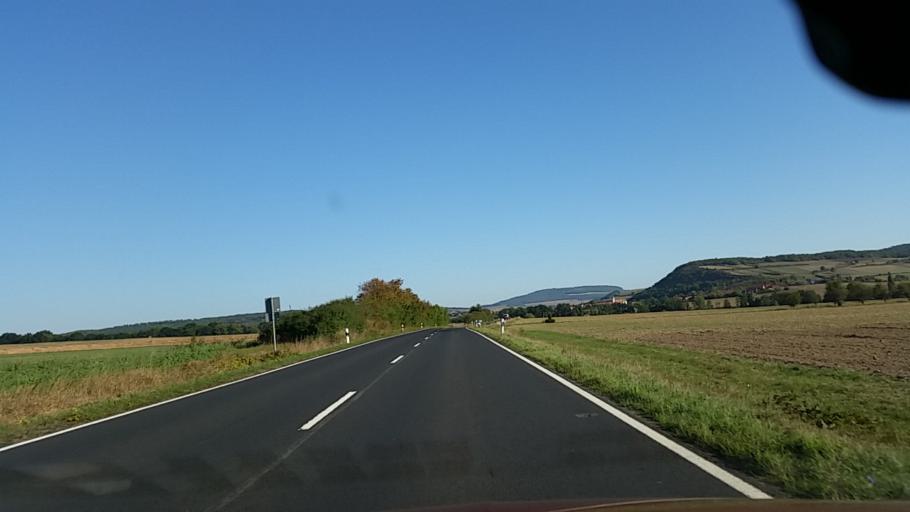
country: DE
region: Bavaria
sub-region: Regierungsbezirk Unterfranken
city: Gossenheim
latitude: 50.0281
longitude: 9.7791
